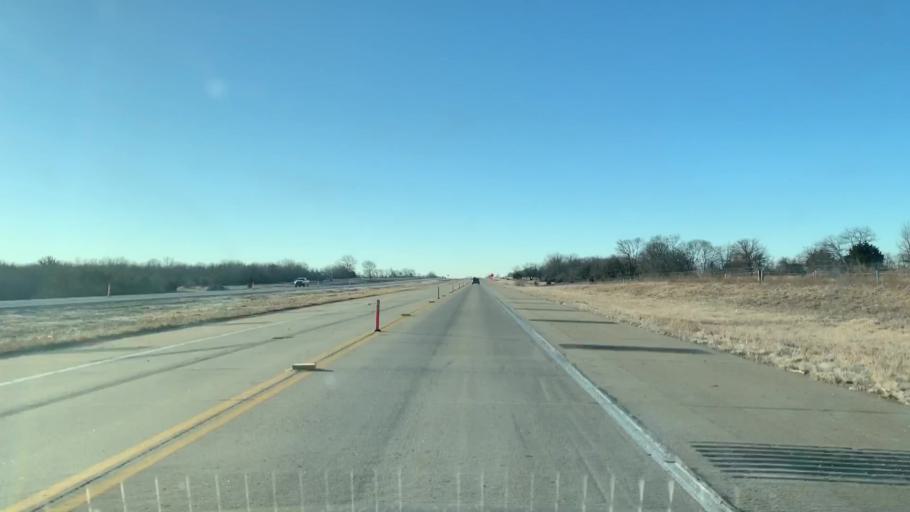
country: US
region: Kansas
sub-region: Bourbon County
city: Fort Scott
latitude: 37.7583
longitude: -94.7050
